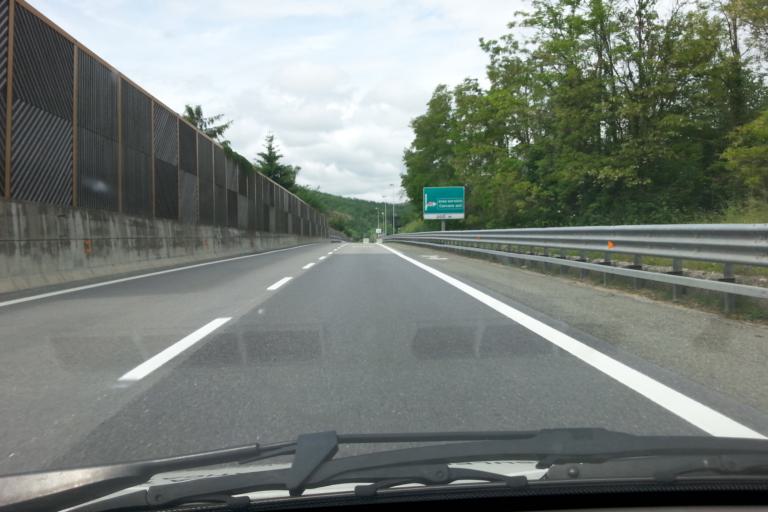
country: IT
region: Liguria
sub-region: Provincia di Savona
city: Carcare
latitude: 44.3476
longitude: 8.3055
